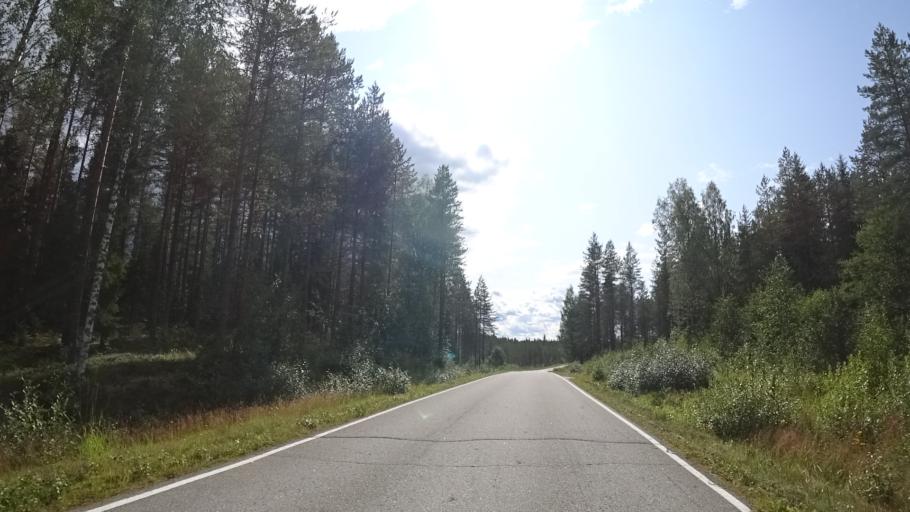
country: FI
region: North Karelia
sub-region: Joensuu
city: Ilomantsi
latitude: 62.4165
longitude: 31.0112
